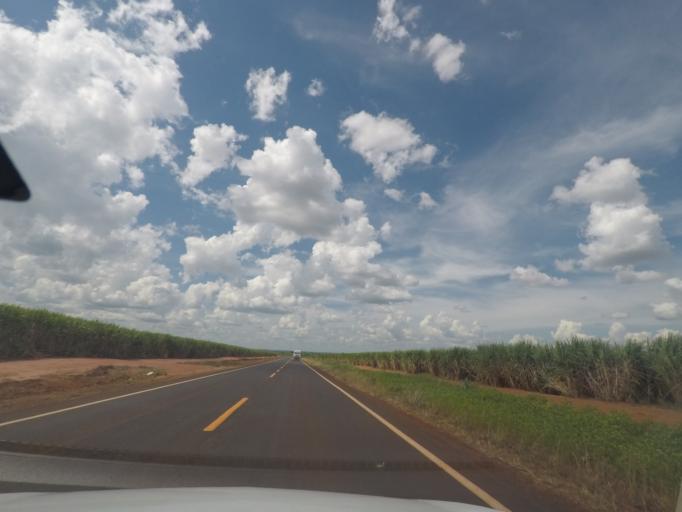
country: BR
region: Minas Gerais
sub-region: Conceicao Das Alagoas
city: Conceicao das Alagoas
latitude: -19.8433
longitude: -48.5936
